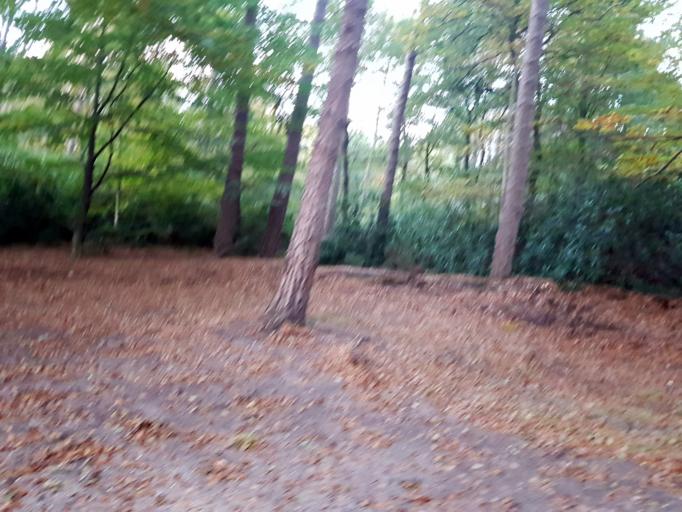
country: NL
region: Utrecht
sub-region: Gemeente Utrechtse Heuvelrug
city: Maarsbergen
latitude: 52.0401
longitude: 5.4034
